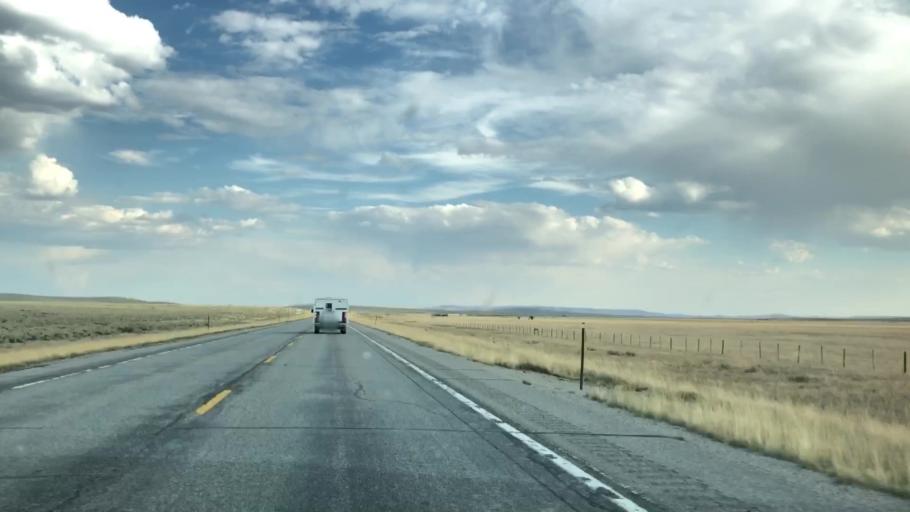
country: US
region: Wyoming
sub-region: Sublette County
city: Pinedale
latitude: 43.0426
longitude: -110.1421
